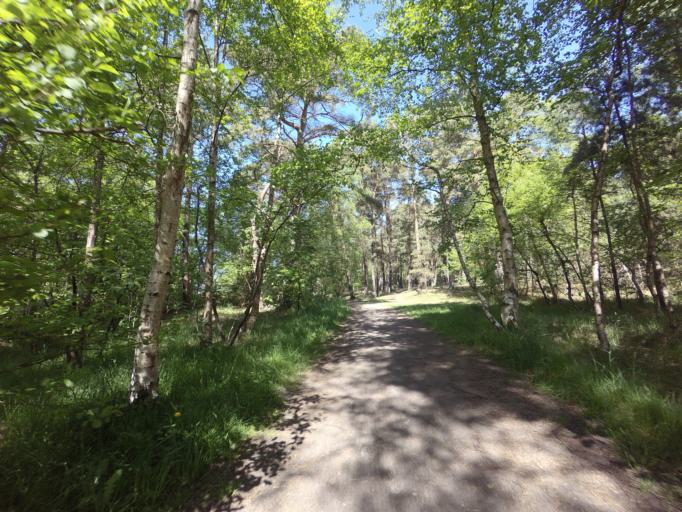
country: SE
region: Skane
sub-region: Vellinge Kommun
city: Hollviken
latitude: 55.4029
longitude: 12.9601
